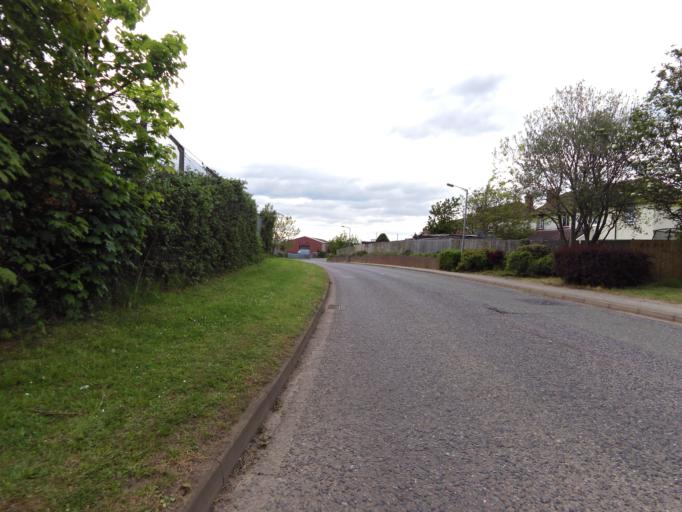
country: GB
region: England
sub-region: Suffolk
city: Ipswich
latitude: 52.0353
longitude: 1.1710
